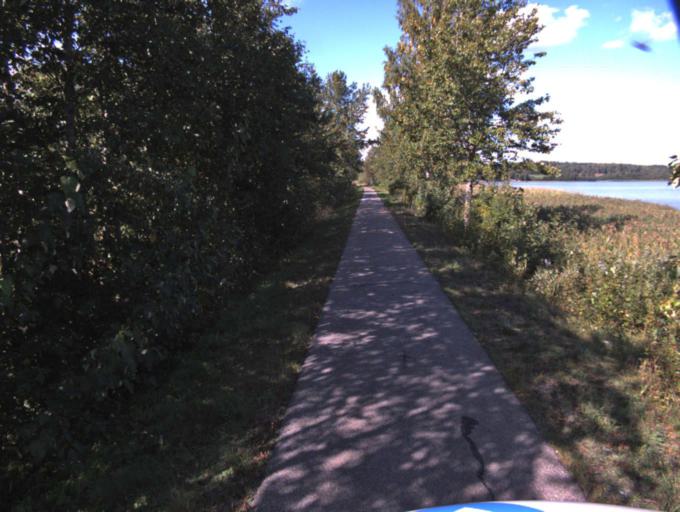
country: SE
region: Vaestra Goetaland
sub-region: Ulricehamns Kommun
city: Ulricehamn
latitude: 57.8422
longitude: 13.3025
